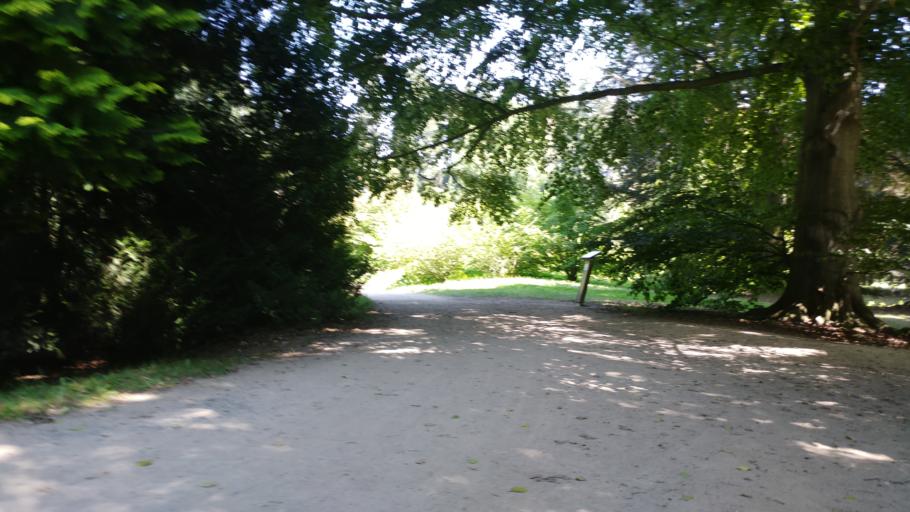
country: CZ
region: Central Bohemia
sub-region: Okres Praha-Zapad
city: Pruhonice
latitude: 49.9969
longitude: 14.5594
